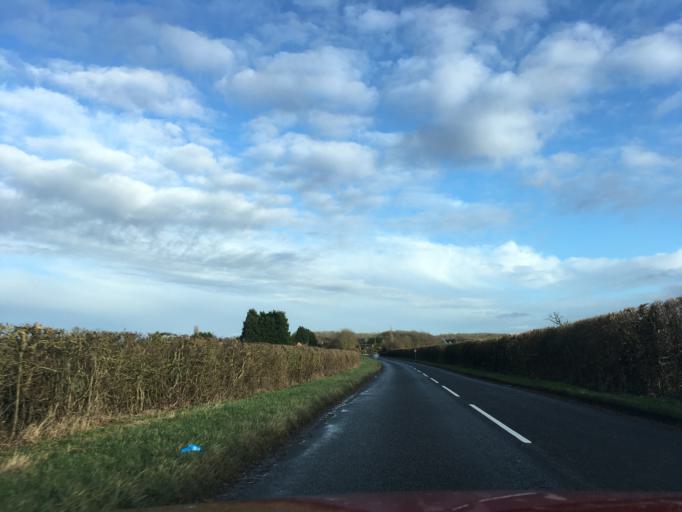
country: GB
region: England
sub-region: Warwickshire
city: Stratford-upon-Avon
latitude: 52.2245
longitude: -1.7468
